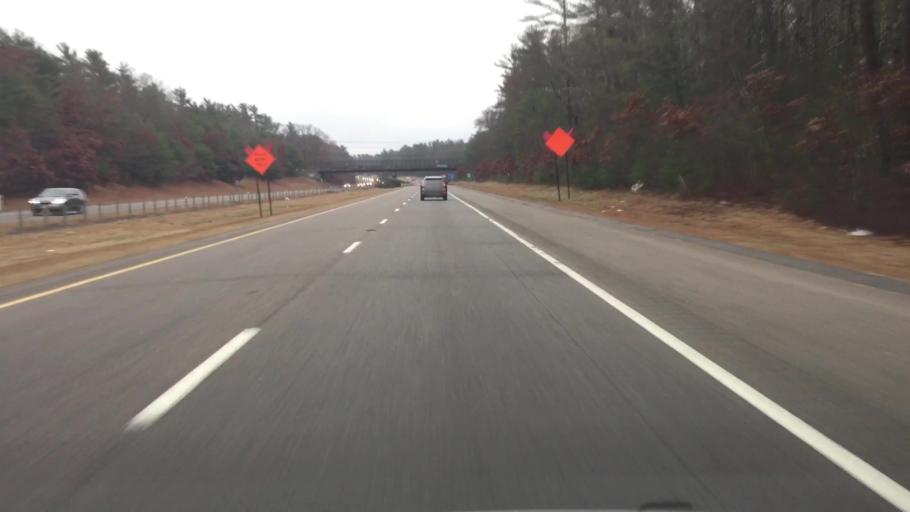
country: US
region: Massachusetts
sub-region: Plymouth County
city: Middleborough Center
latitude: 41.8509
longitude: -70.8620
